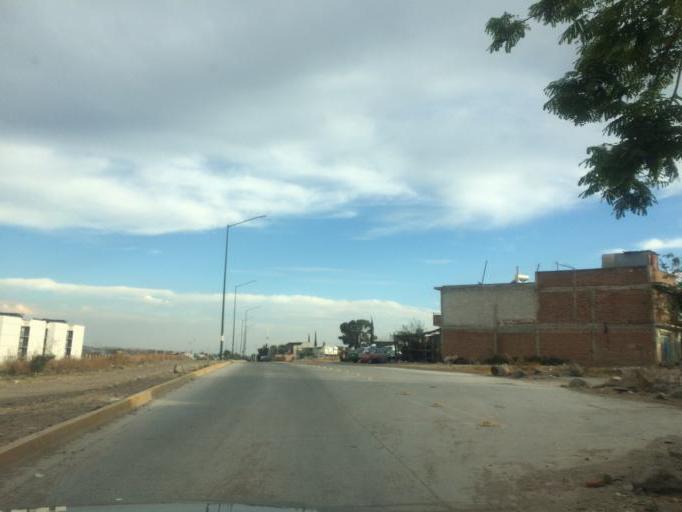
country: MX
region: Guanajuato
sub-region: Leon
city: Rizos de la Joya (Rizos del Saucillo)
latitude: 21.1435
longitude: -101.7541
